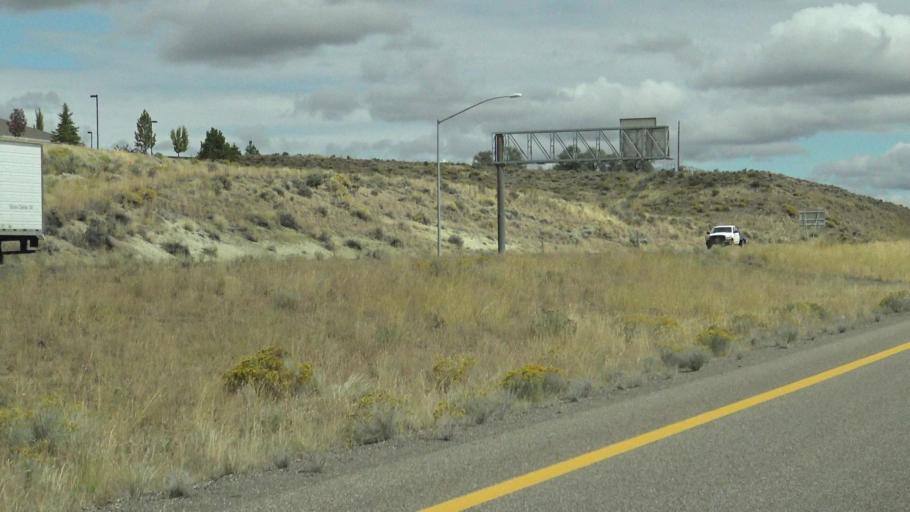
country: US
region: Nevada
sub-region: Elko County
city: Elko
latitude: 40.8557
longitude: -115.7432
